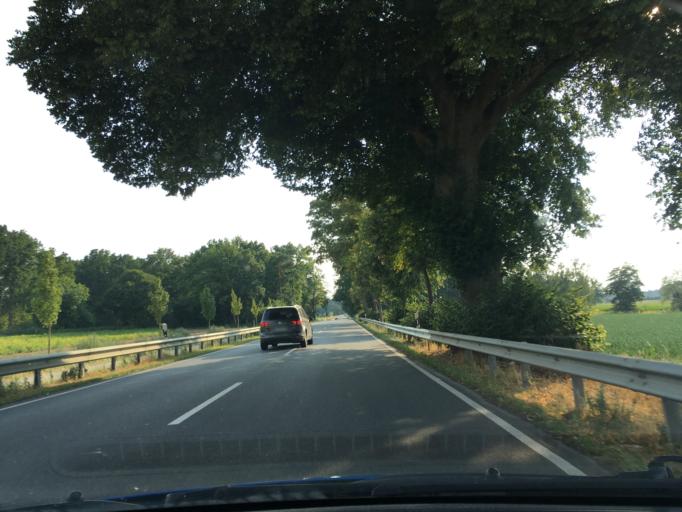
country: DE
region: Lower Saxony
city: Zernien
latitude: 53.0630
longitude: 10.8539
